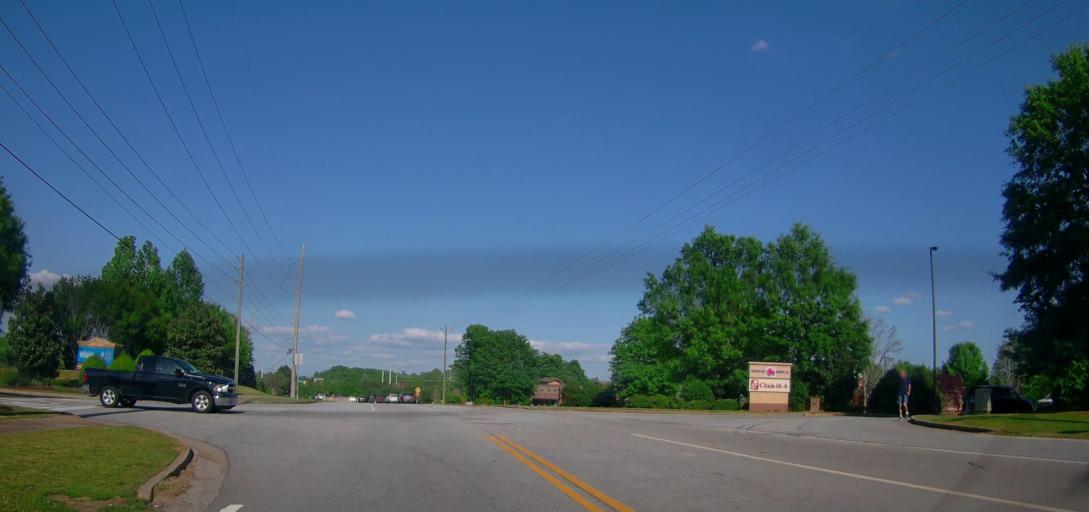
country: US
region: Georgia
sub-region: Morgan County
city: Madison
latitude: 33.5640
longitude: -83.4805
